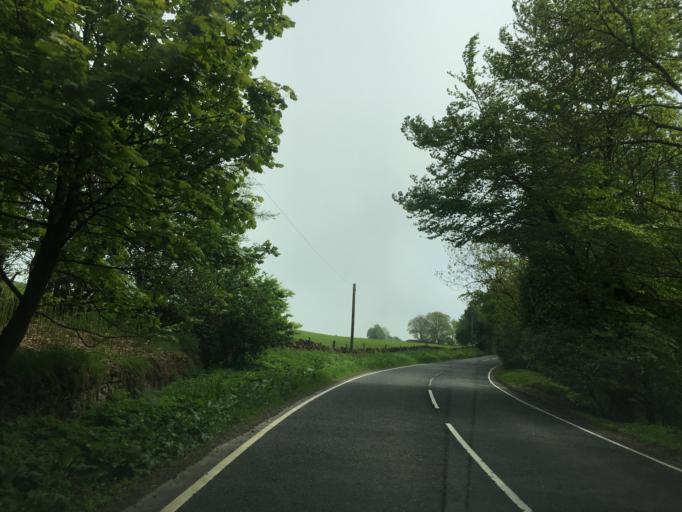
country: GB
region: Scotland
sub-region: The Scottish Borders
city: West Linton
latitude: 55.7026
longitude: -3.3621
